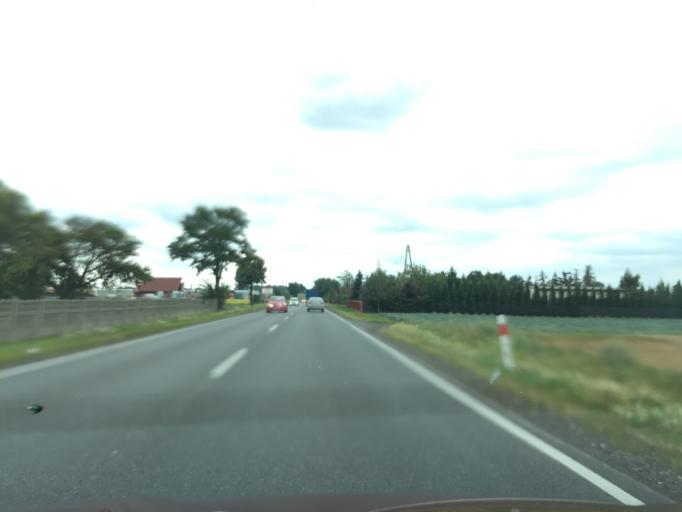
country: PL
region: Greater Poland Voivodeship
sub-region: Kalisz
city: Kalisz
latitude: 51.8284
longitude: 18.0946
